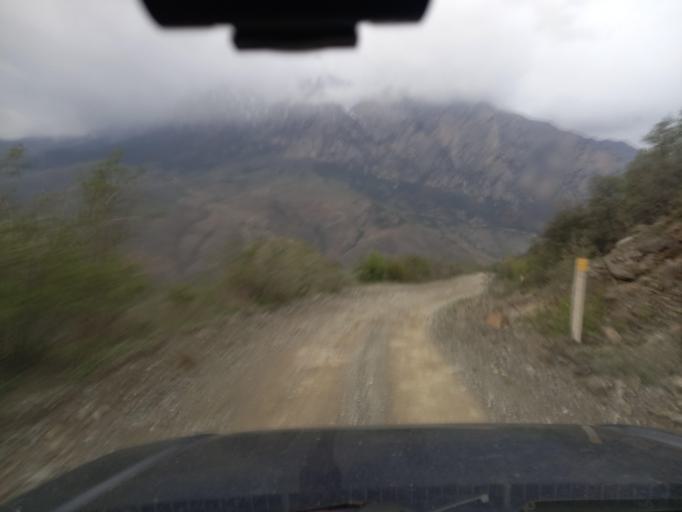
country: RU
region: North Ossetia
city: Mizur
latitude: 42.8496
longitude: 44.1628
